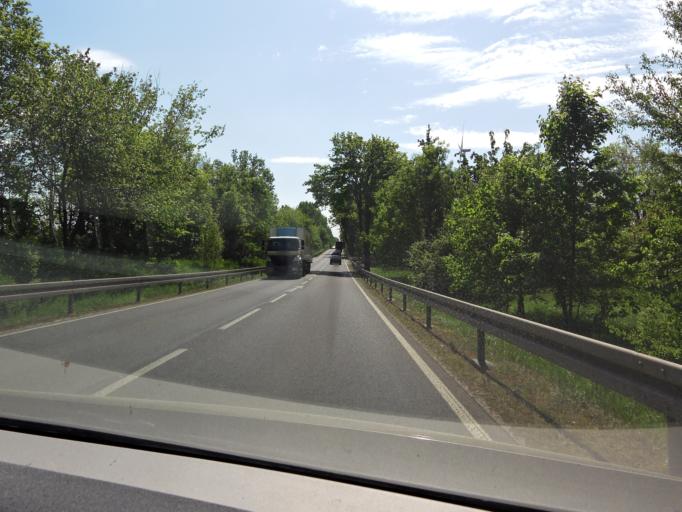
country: DE
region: Thuringia
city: Hochheim
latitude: 51.0344
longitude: 10.6691
